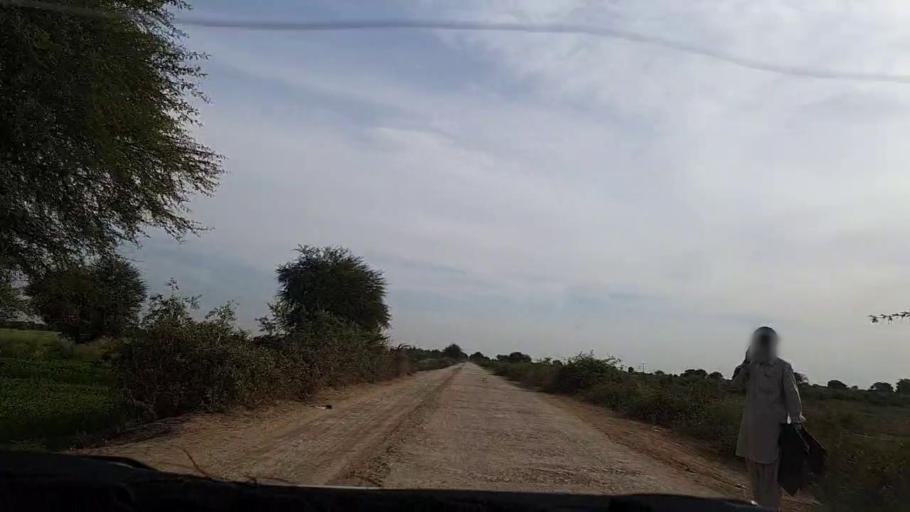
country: PK
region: Sindh
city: Dhoro Naro
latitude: 25.4269
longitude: 69.5217
